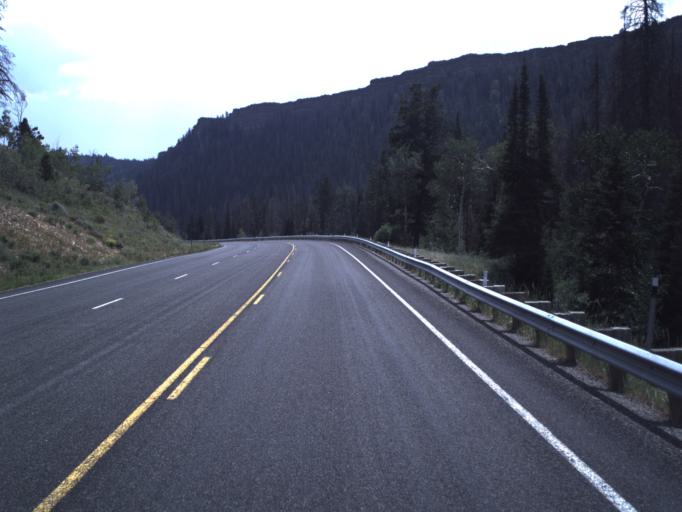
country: US
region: Utah
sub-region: Summit County
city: Francis
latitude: 40.4798
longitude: -110.9420
